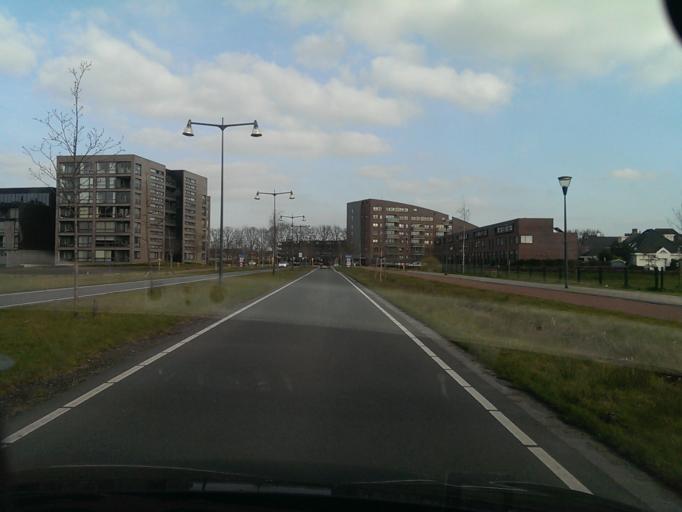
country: NL
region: North Brabant
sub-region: Gemeente Eindhoven
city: Meerhoven
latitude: 51.4334
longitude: 5.3996
